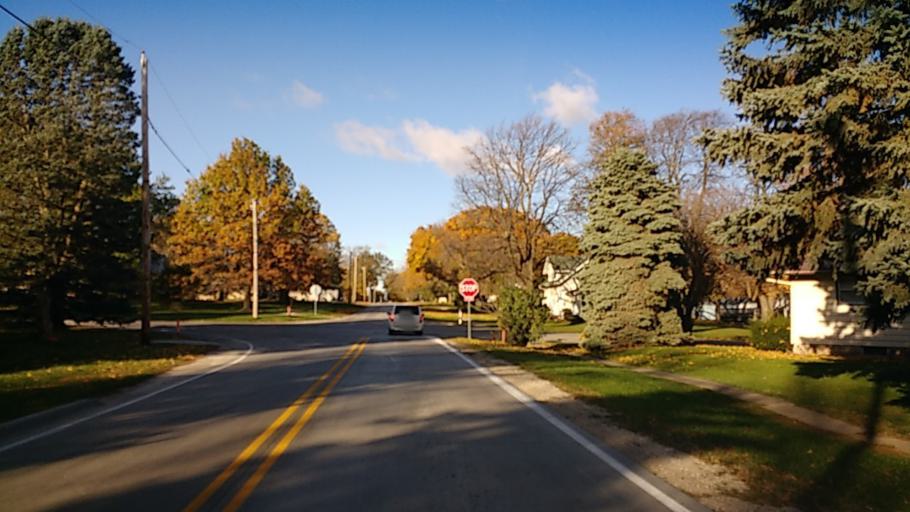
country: US
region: Iowa
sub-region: Ida County
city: Holstein
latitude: 42.5038
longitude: -95.4167
